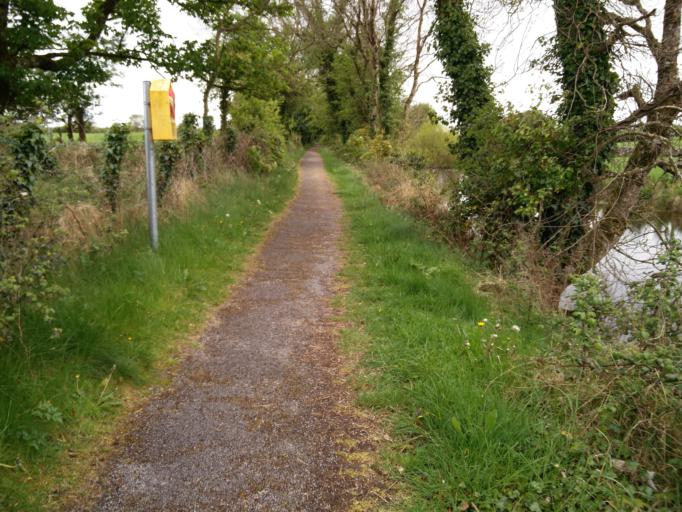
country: IE
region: Connaught
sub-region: Maigh Eo
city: Ballinrobe
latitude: 53.6262
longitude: -9.2403
